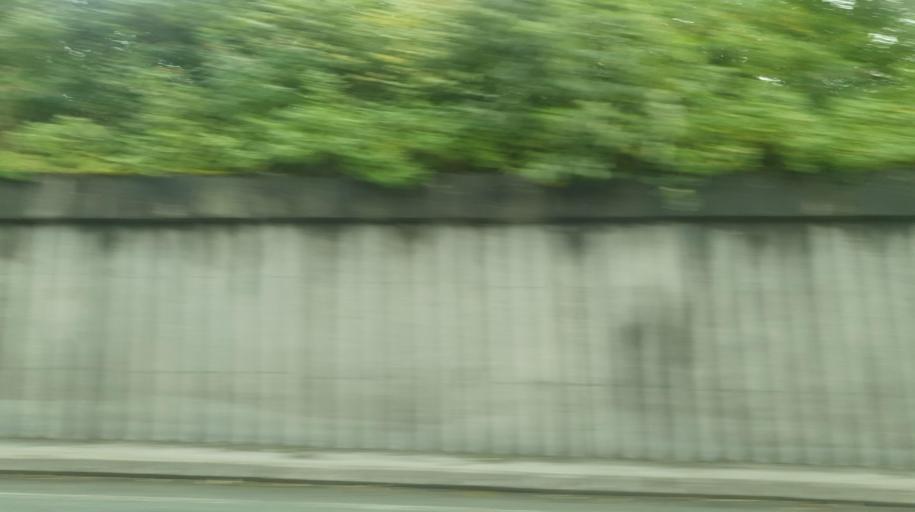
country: NO
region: Nord-Trondelag
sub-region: Verdal
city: Verdal
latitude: 63.7889
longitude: 11.4857
